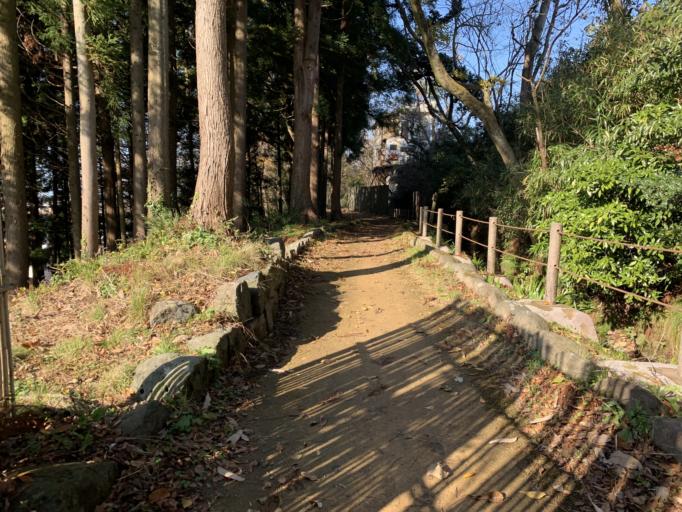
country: JP
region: Ishikawa
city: Nonoichi
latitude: 36.5379
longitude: 136.6870
